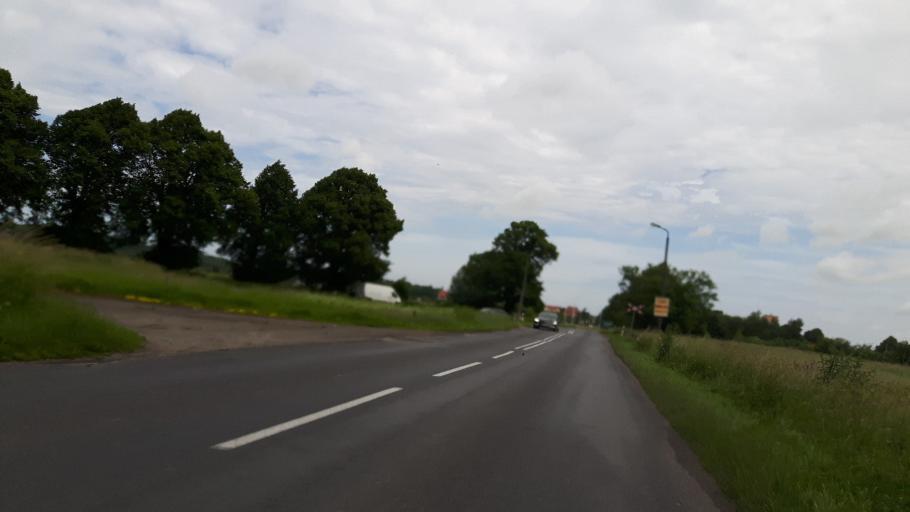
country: PL
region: West Pomeranian Voivodeship
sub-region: Powiat gryficki
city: Trzebiatow
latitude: 54.0473
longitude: 15.2530
